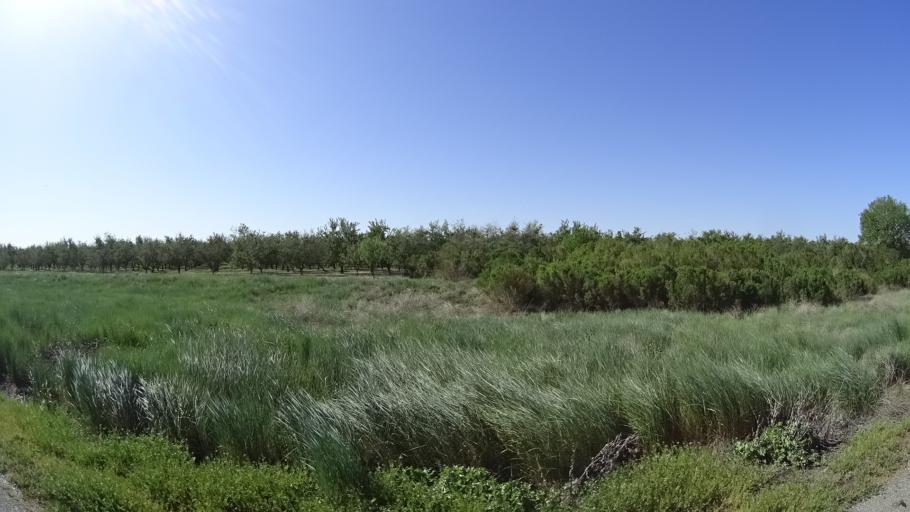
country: US
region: California
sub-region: Glenn County
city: Hamilton City
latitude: 39.7129
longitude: -121.9899
